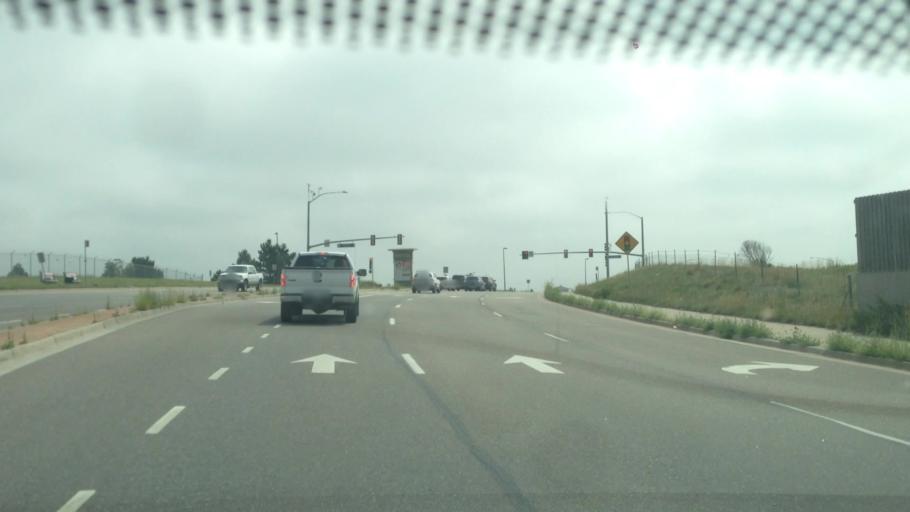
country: US
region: Colorado
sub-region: Douglas County
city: Parker
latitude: 39.6022
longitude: -104.7184
